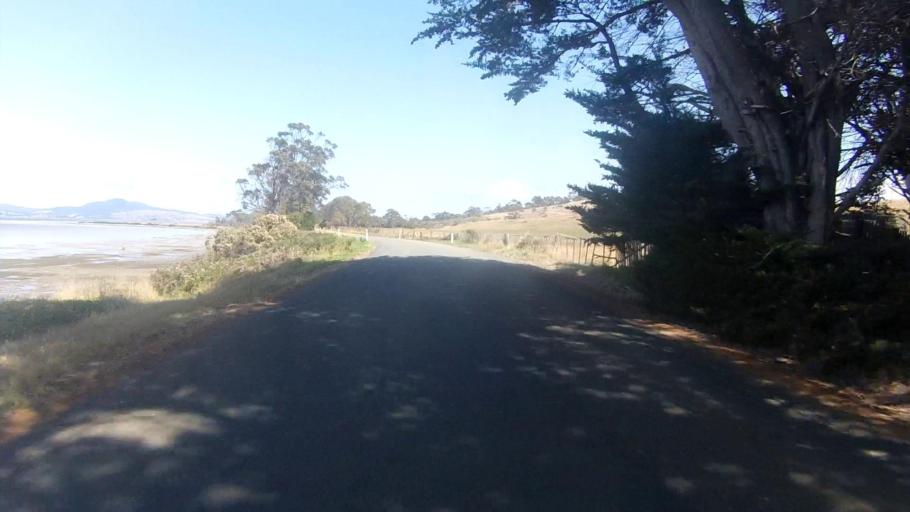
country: AU
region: Tasmania
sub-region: Sorell
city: Sorell
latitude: -42.8294
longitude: 147.8575
